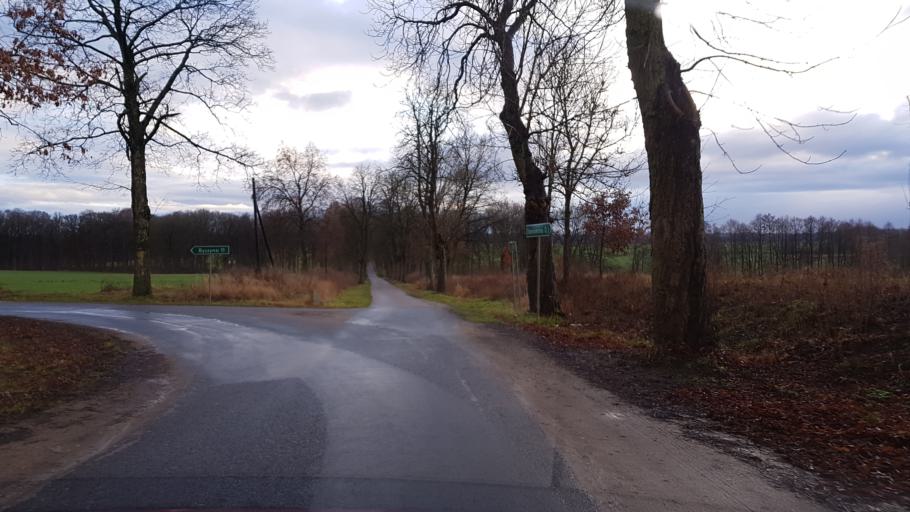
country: PL
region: West Pomeranian Voivodeship
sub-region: Powiat bialogardzki
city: Karlino
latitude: 53.9537
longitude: 15.8981
